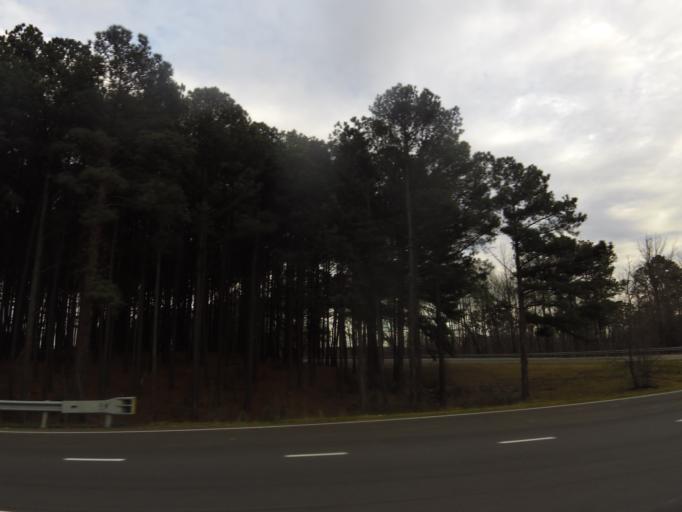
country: US
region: North Carolina
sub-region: Nash County
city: Rocky Mount
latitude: 35.9648
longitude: -77.8180
